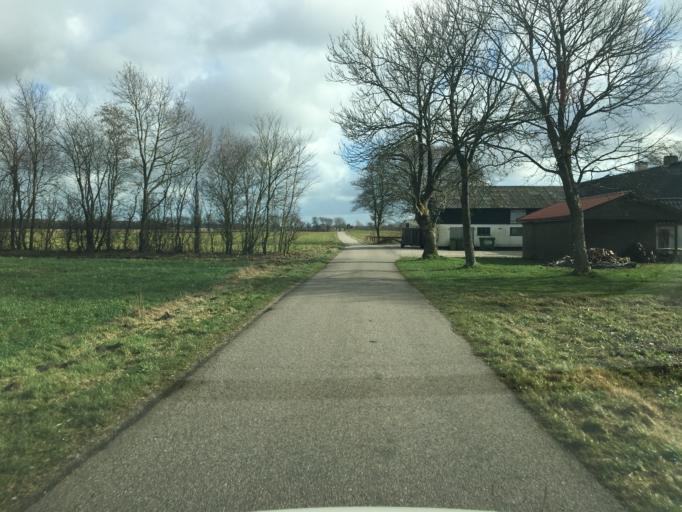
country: DK
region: South Denmark
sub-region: Aabenraa Kommune
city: Krusa
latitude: 54.9157
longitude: 9.3668
